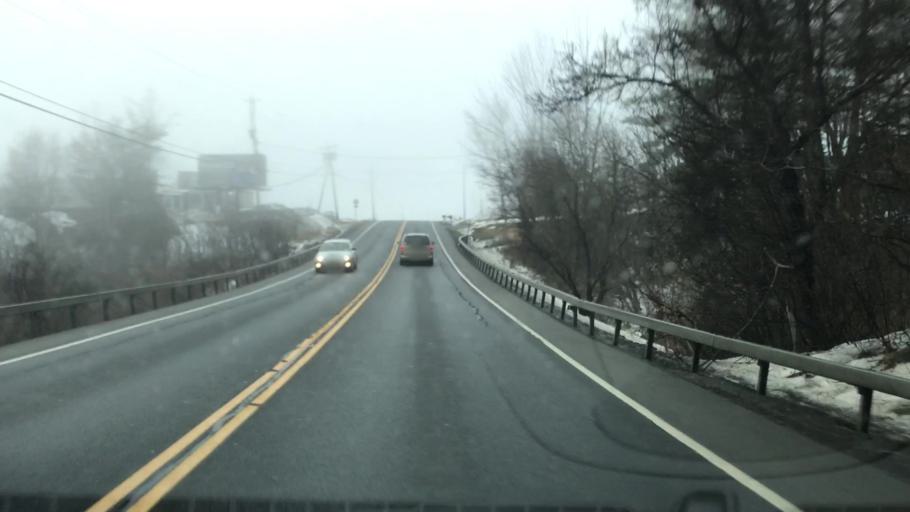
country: US
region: New York
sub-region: Washington County
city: Whitehall
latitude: 43.5348
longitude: -73.4106
